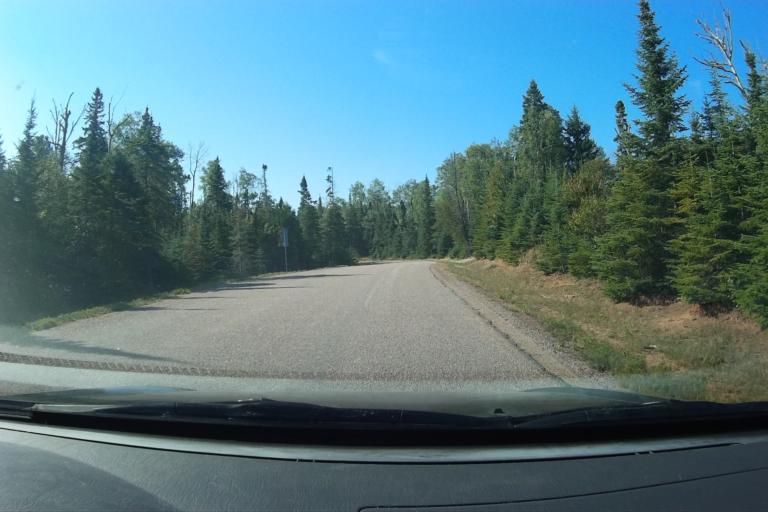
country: CA
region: Ontario
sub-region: Thunder Bay District
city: Thunder Bay
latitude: 48.3531
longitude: -88.8050
